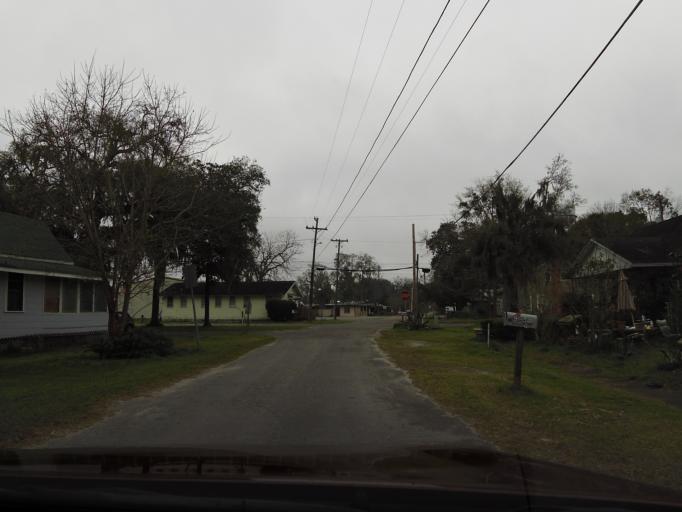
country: US
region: Florida
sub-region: Alachua County
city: High Springs
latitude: 29.8257
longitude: -82.5994
